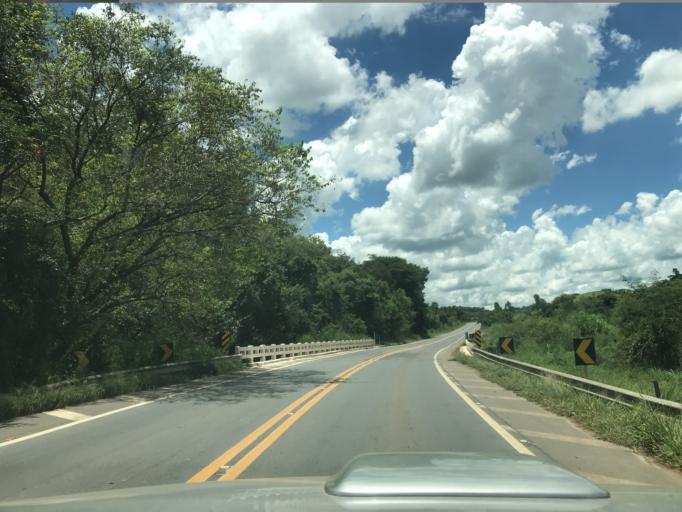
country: BR
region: Minas Gerais
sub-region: Perdoes
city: Perdoes
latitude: -21.0946
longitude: -45.1011
